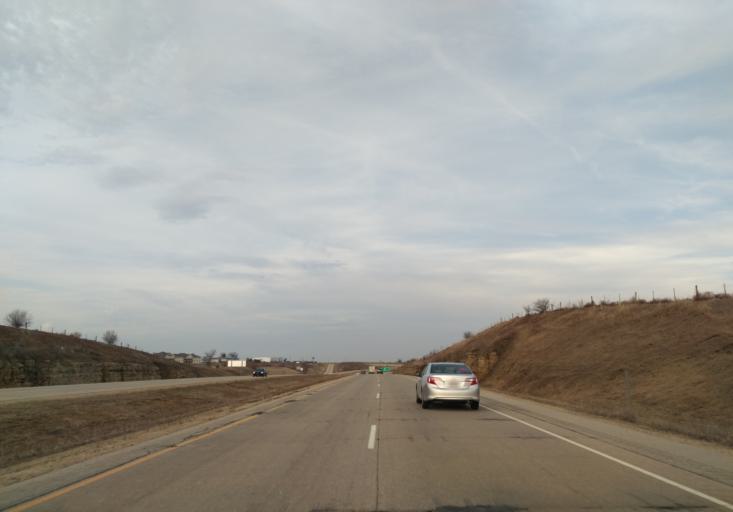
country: US
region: Wisconsin
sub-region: Dane County
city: Mount Horeb
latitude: 43.0001
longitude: -89.7126
